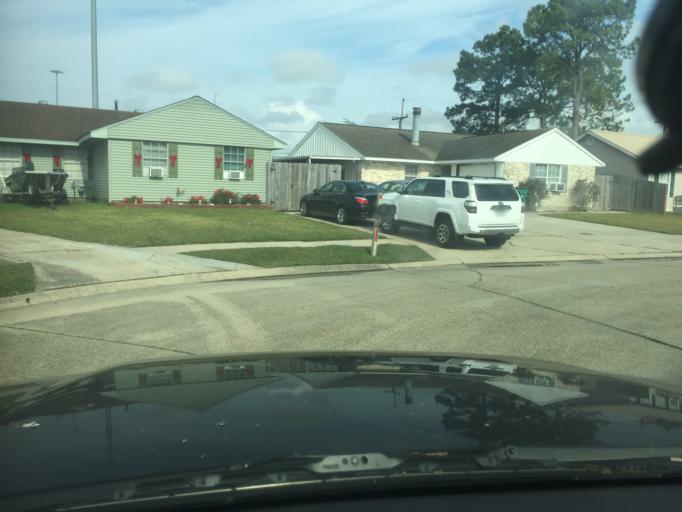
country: US
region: Louisiana
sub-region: Jefferson Parish
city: Avondale
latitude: 29.9161
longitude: -90.2034
